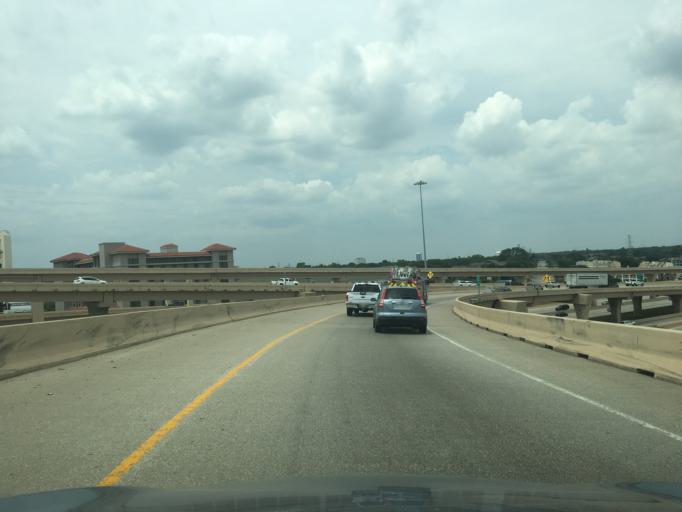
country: US
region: Texas
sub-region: Dallas County
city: Richardson
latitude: 32.9254
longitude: -96.7608
